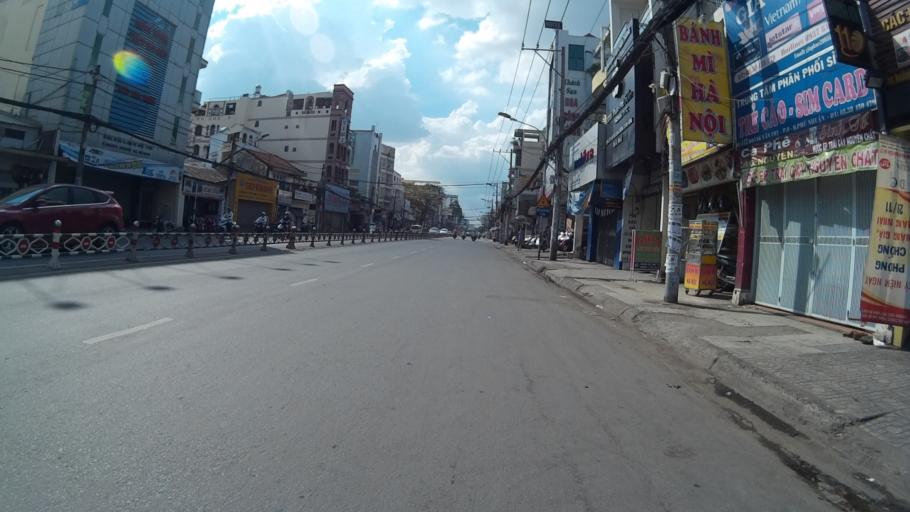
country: VN
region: Ho Chi Minh City
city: Quan Phu Nhuan
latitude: 10.7995
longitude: 106.6773
